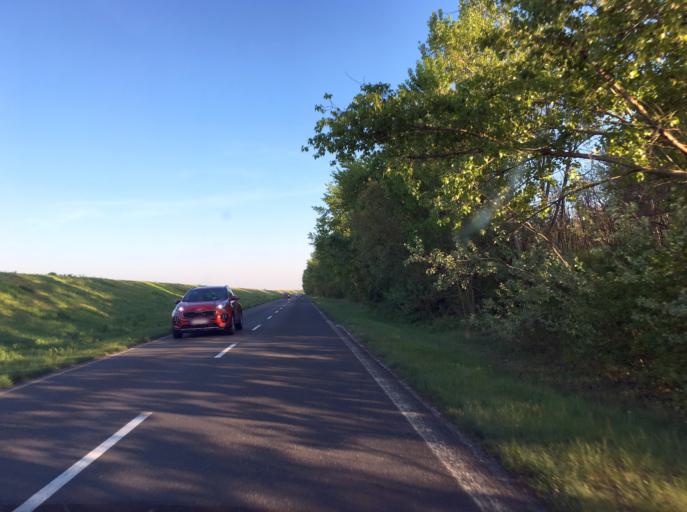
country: HU
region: Gyor-Moson-Sopron
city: Rajka
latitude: 48.0233
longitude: 17.2461
